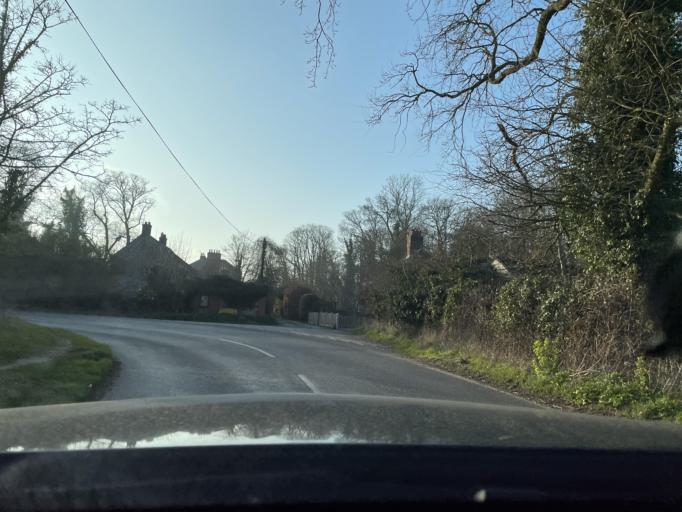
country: GB
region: England
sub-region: Norfolk
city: Martham
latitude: 52.7477
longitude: 1.6420
